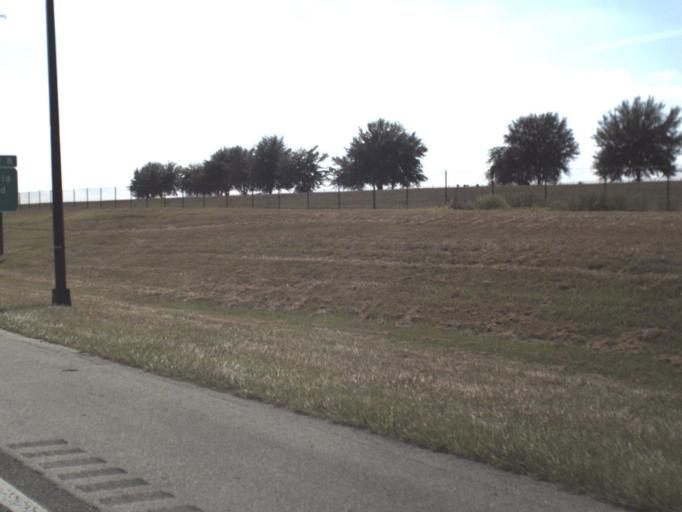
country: US
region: Florida
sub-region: Polk County
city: Citrus Ridge
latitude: 28.3982
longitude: -81.6217
